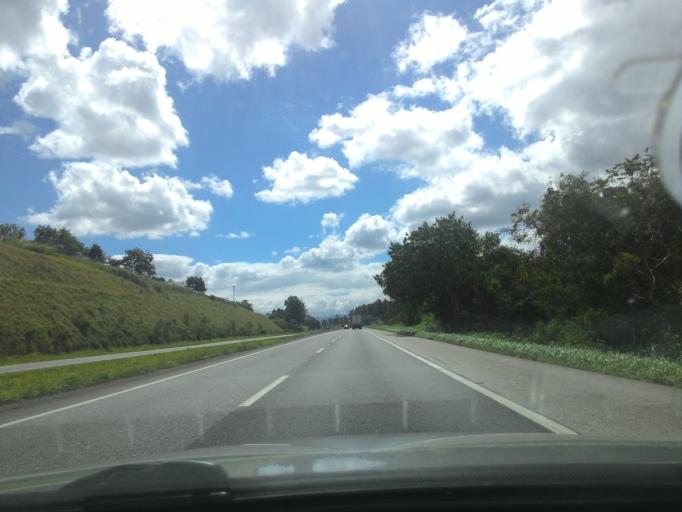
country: BR
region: Sao Paulo
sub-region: Cajati
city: Cajati
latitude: -24.7216
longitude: -48.0734
